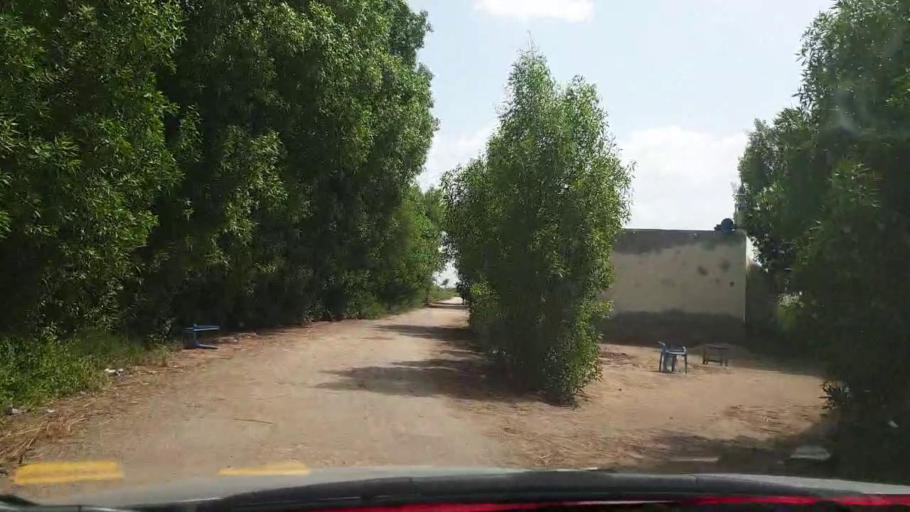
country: PK
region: Sindh
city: Tando Bago
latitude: 24.8717
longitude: 68.9155
